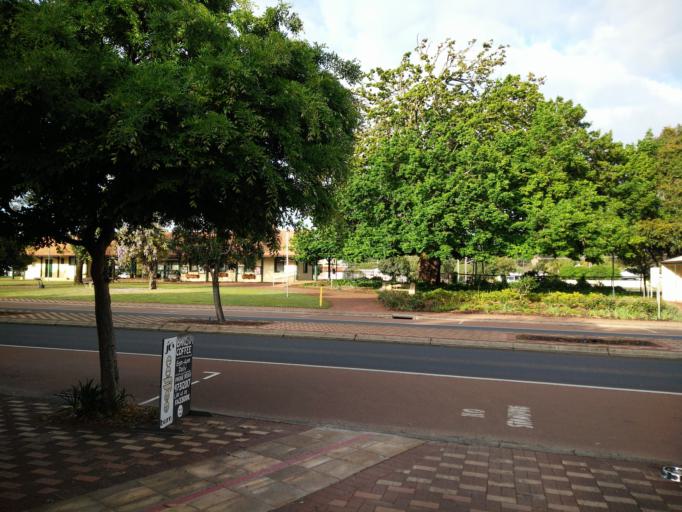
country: AU
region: Western Australia
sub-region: Donnybrook-Balingup
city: Donnybrook
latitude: -33.5727
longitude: 115.8242
